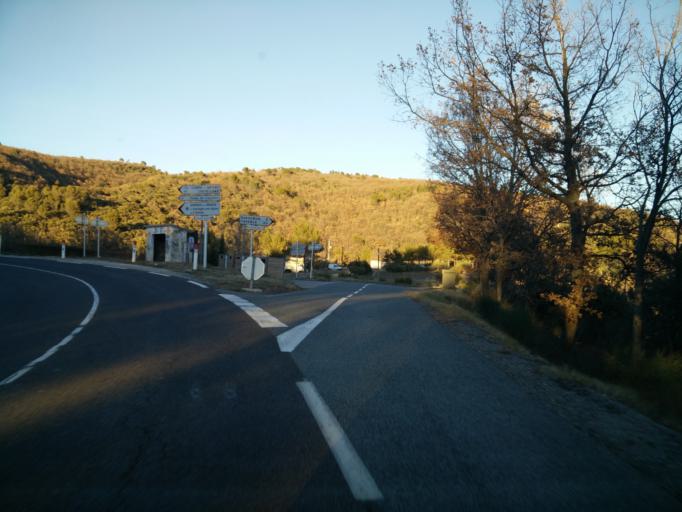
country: FR
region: Provence-Alpes-Cote d'Azur
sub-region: Departement du Var
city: Montferrat
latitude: 43.6293
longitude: 6.4936
